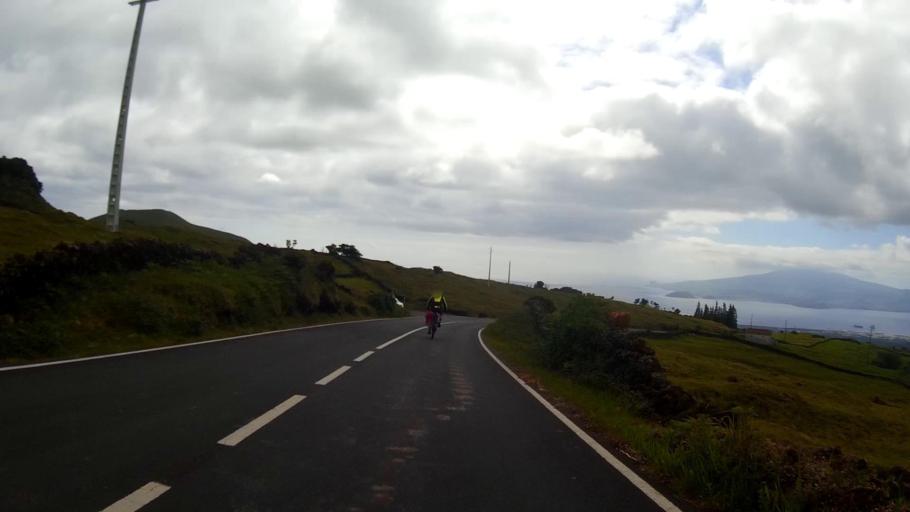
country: PT
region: Azores
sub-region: Madalena
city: Madalena
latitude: 38.4965
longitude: -28.4458
